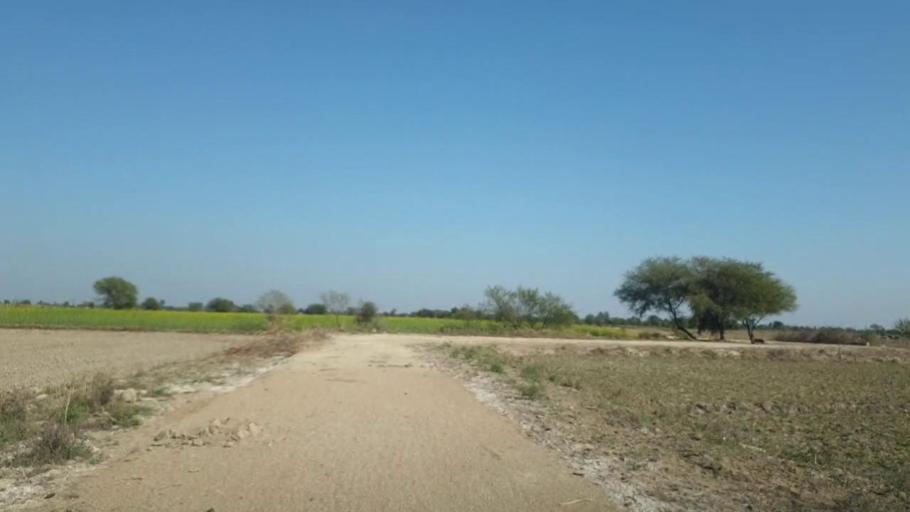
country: PK
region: Sindh
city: Mirpur Khas
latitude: 25.6276
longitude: 69.0407
